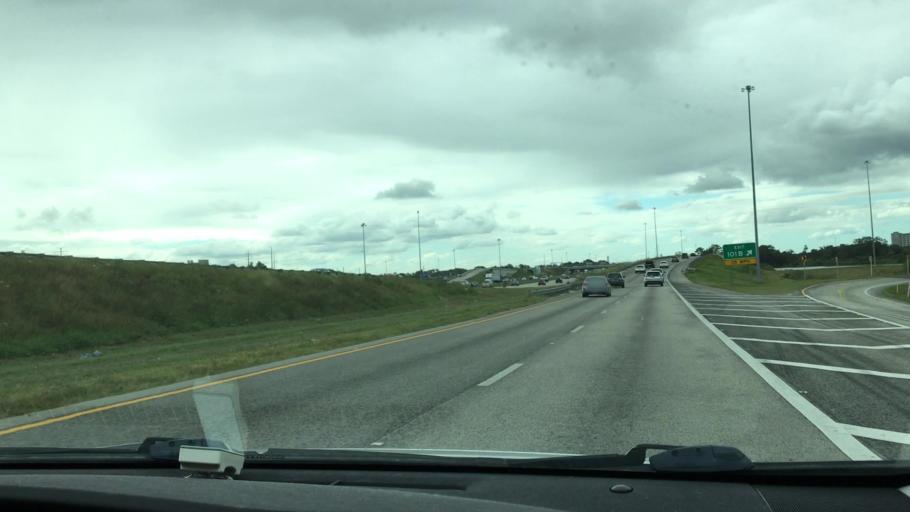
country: US
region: Florida
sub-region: Seminole County
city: Heathrow
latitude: 28.7945
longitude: -81.3470
